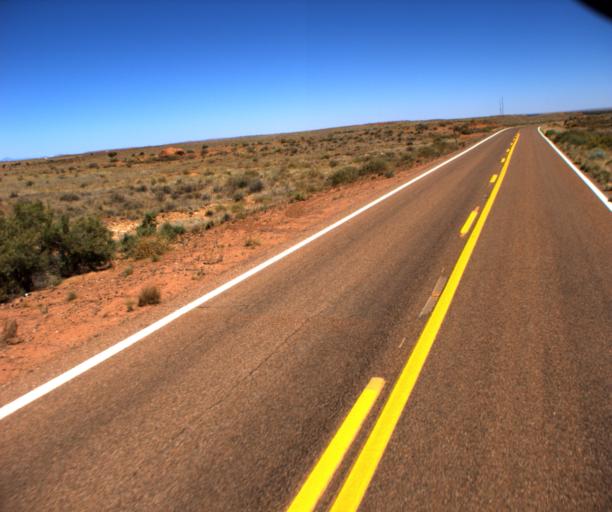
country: US
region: Arizona
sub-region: Navajo County
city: Winslow
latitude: 34.9497
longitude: -110.6463
